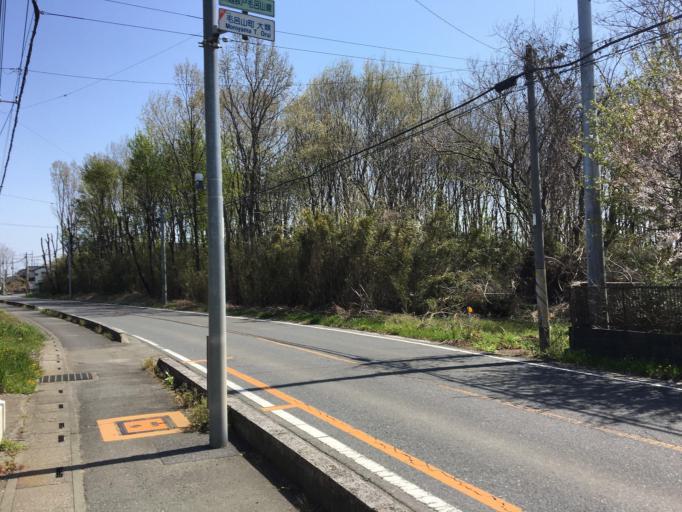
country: JP
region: Saitama
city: Sakado
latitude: 35.9551
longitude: 139.3466
